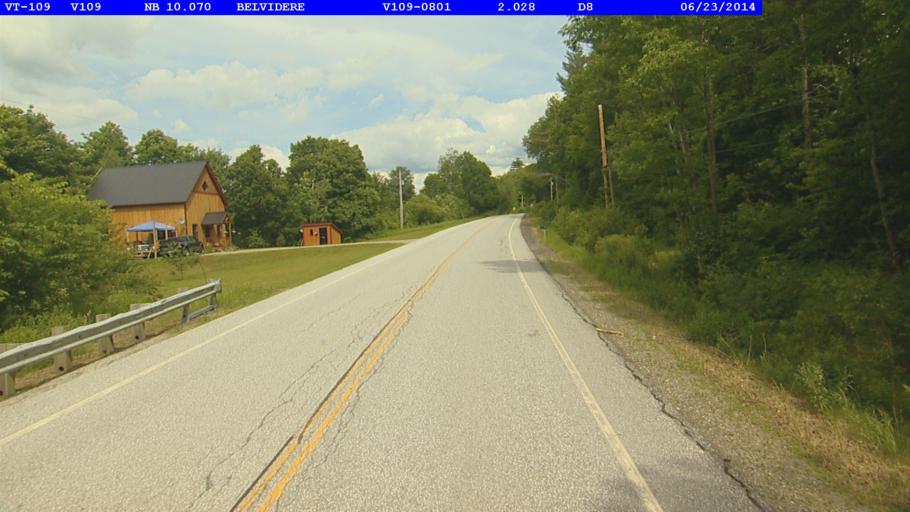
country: US
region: Vermont
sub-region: Lamoille County
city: Johnson
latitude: 44.7468
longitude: -72.7065
